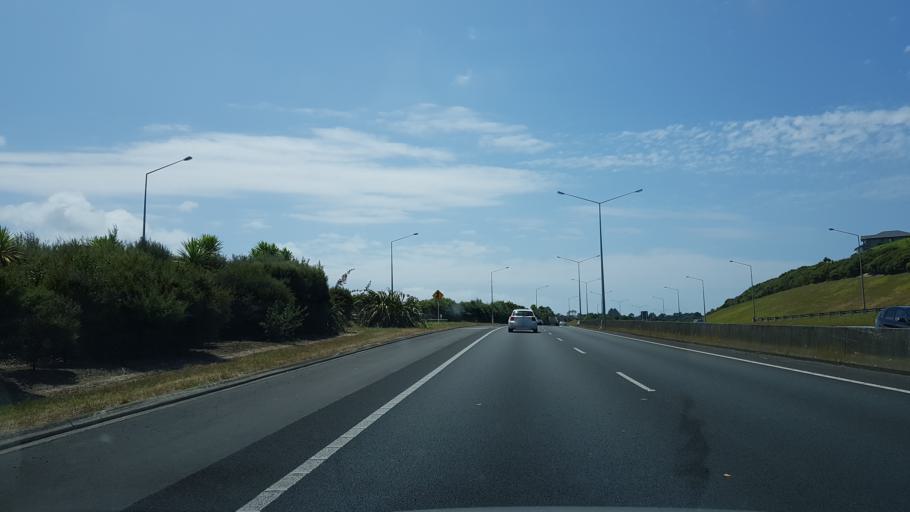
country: NZ
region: Auckland
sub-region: Auckland
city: North Shore
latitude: -36.7707
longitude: 174.6862
